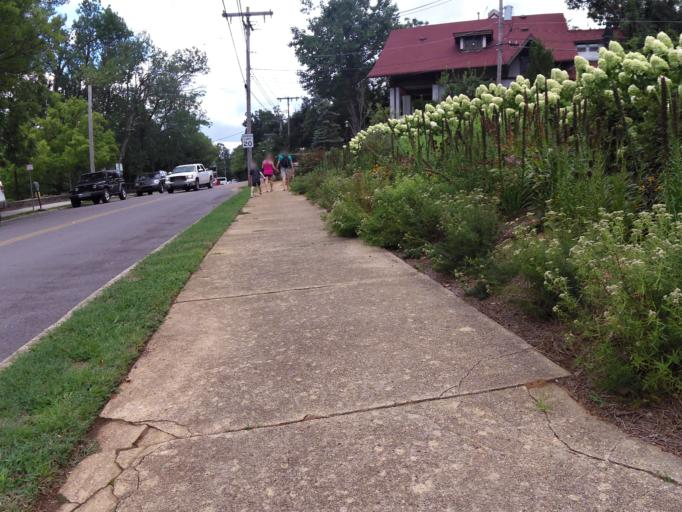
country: US
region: Tennessee
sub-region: Hamilton County
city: Lookout Mountain
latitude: 35.0071
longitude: -85.3435
